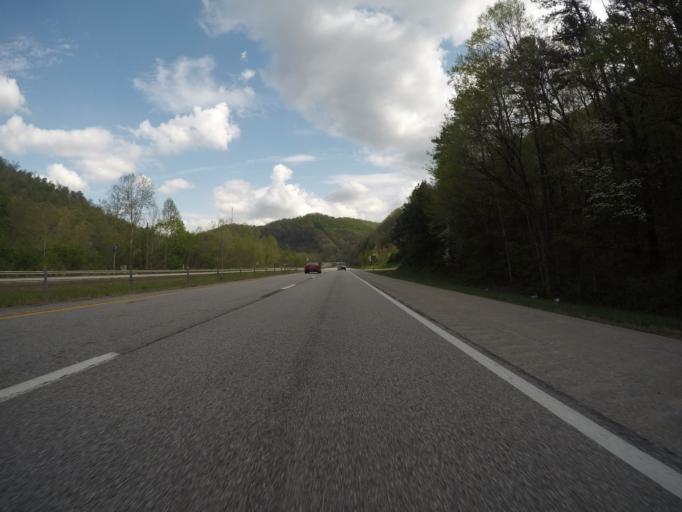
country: US
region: West Virginia
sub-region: Boone County
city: Madison
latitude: 38.1456
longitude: -81.8450
